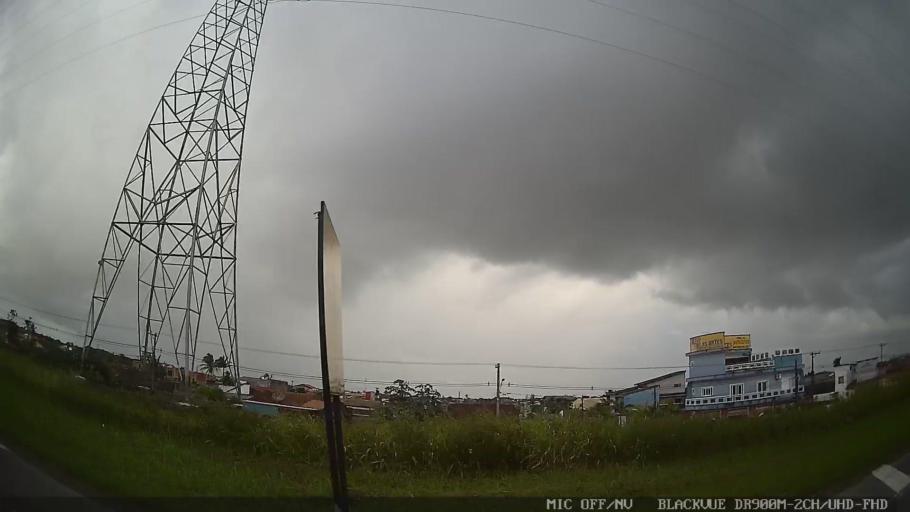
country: BR
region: Sao Paulo
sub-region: Itanhaem
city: Itanhaem
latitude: -24.1974
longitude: -46.8411
